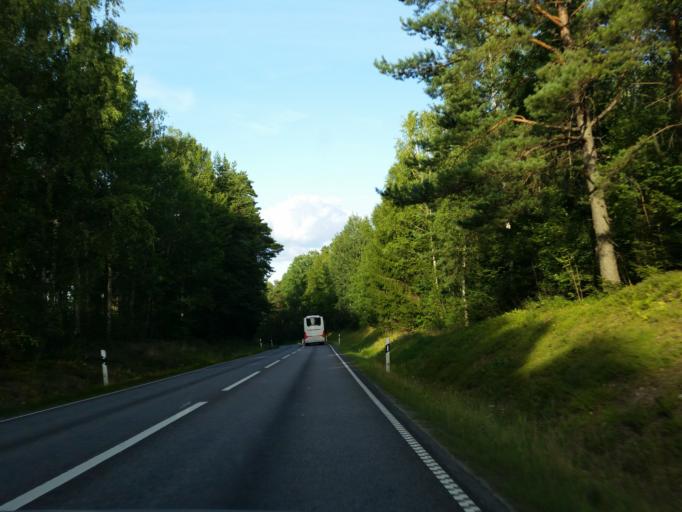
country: SE
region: Stockholm
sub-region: Sodertalje Kommun
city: Molnbo
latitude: 59.0397
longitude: 17.3900
